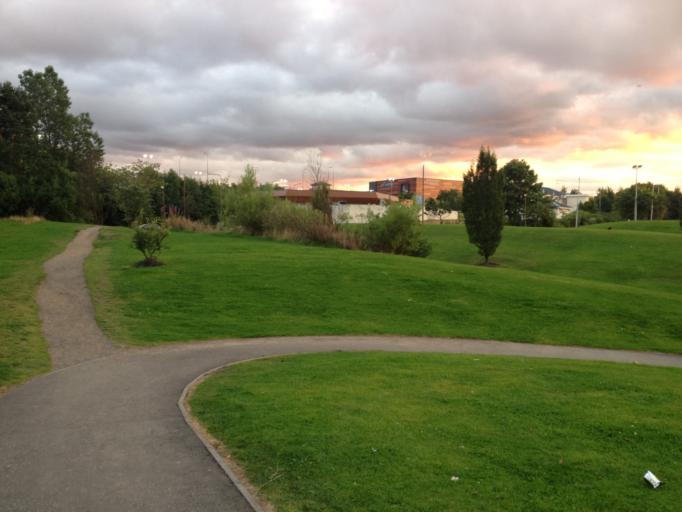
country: GB
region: Scotland
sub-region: West Lothian
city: Livingston
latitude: 55.8880
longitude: -3.5101
